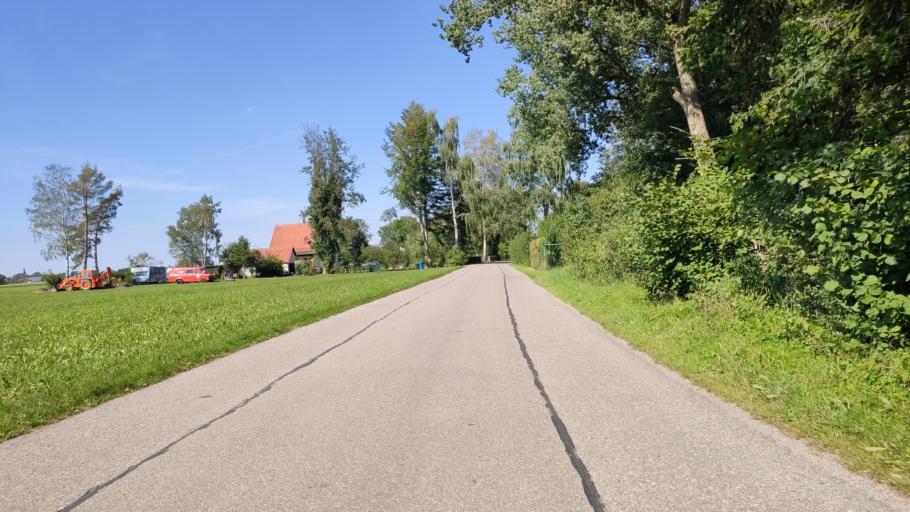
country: DE
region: Bavaria
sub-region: Swabia
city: Konigsbrunn
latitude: 48.2391
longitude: 10.9017
